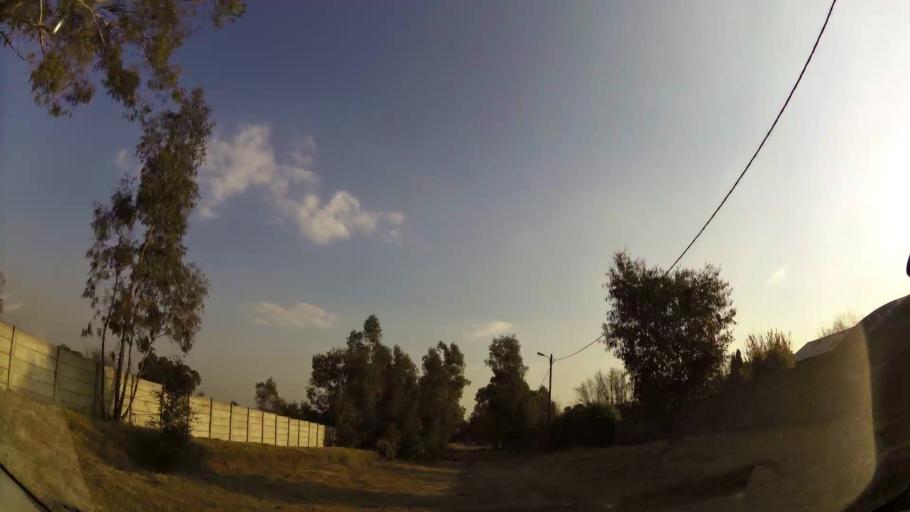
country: ZA
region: Gauteng
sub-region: Ekurhuleni Metropolitan Municipality
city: Benoni
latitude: -26.1535
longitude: 28.3687
